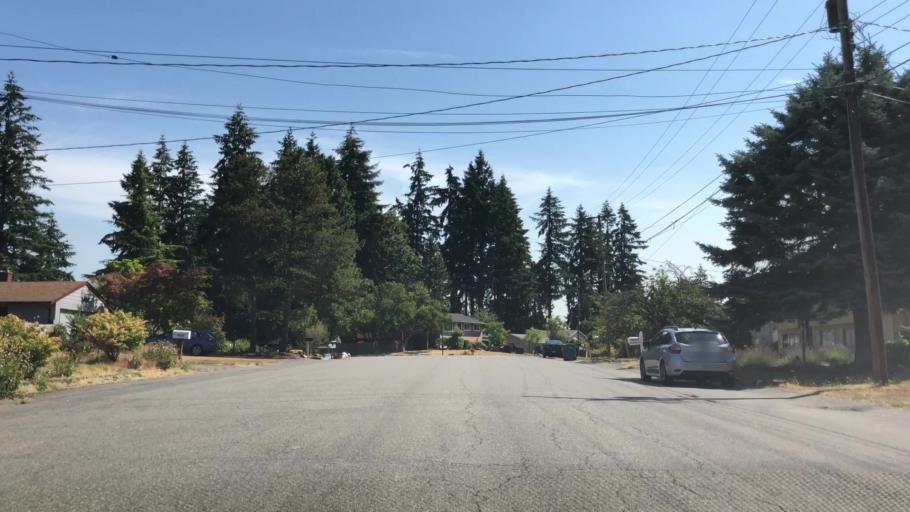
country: US
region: Washington
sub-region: King County
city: Inglewood-Finn Hill
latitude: 47.7320
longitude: -122.2438
